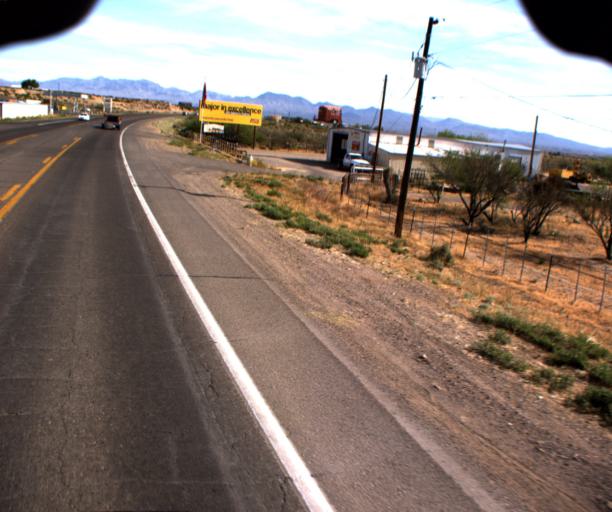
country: US
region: Arizona
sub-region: Graham County
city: Cactus Flat
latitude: 32.7780
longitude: -109.7160
